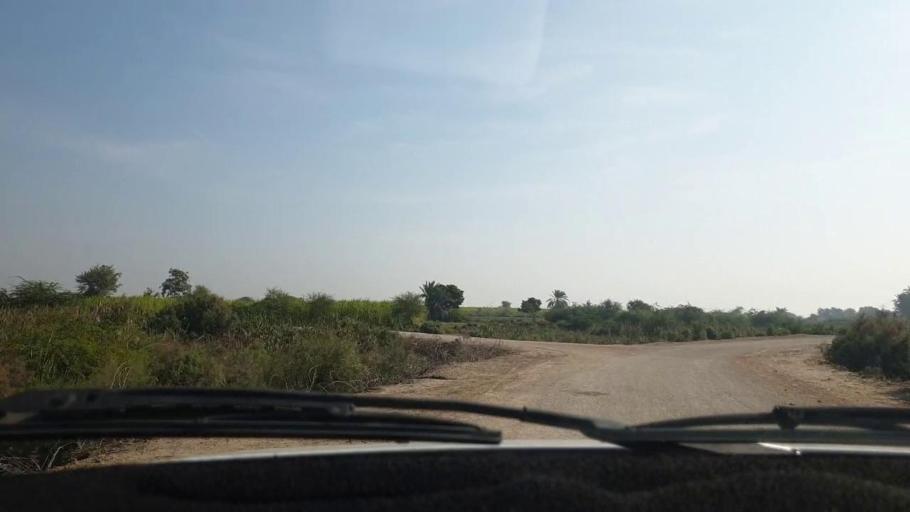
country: PK
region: Sindh
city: Tando Muhammad Khan
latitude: 24.9911
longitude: 68.4645
